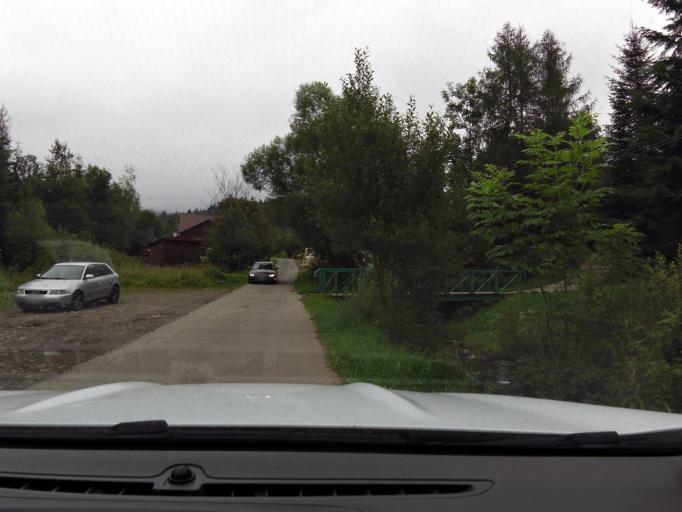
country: PL
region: Silesian Voivodeship
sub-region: Powiat zywiecki
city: Ujsoly
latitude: 49.4941
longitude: 19.1743
